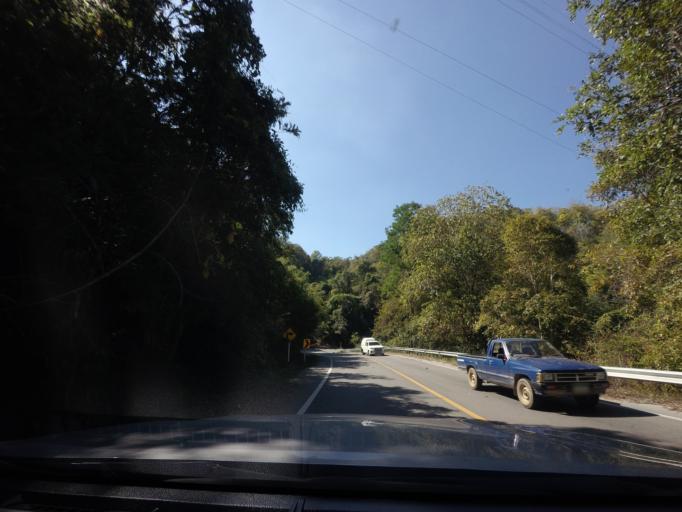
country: TH
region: Lampang
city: Chae Hom
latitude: 18.6353
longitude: 99.6097
